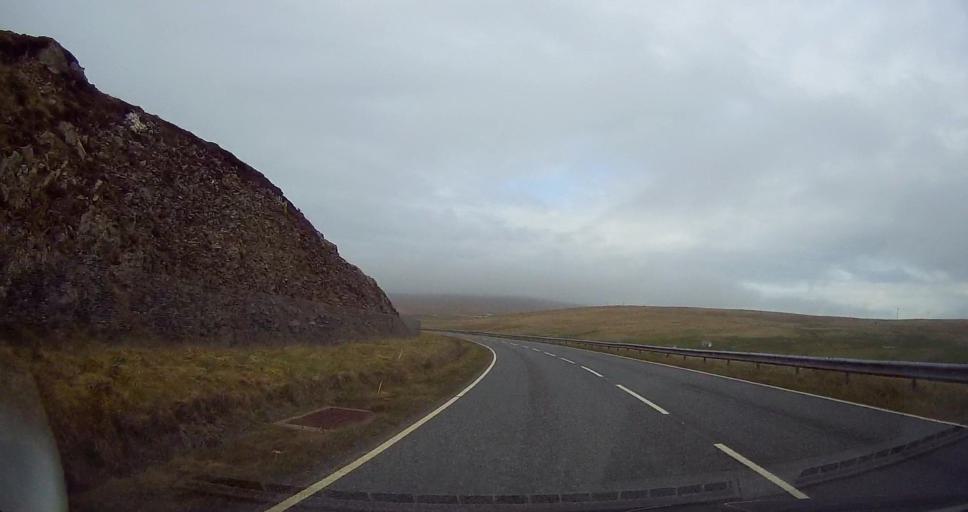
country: GB
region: Scotland
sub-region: Shetland Islands
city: Sandwick
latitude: 59.9932
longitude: -1.2790
